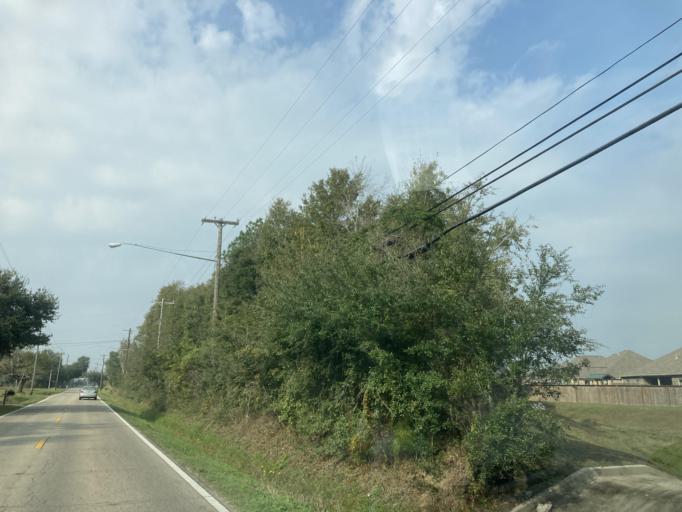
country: US
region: Mississippi
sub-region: Harrison County
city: Long Beach
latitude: 30.3691
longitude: -89.1584
